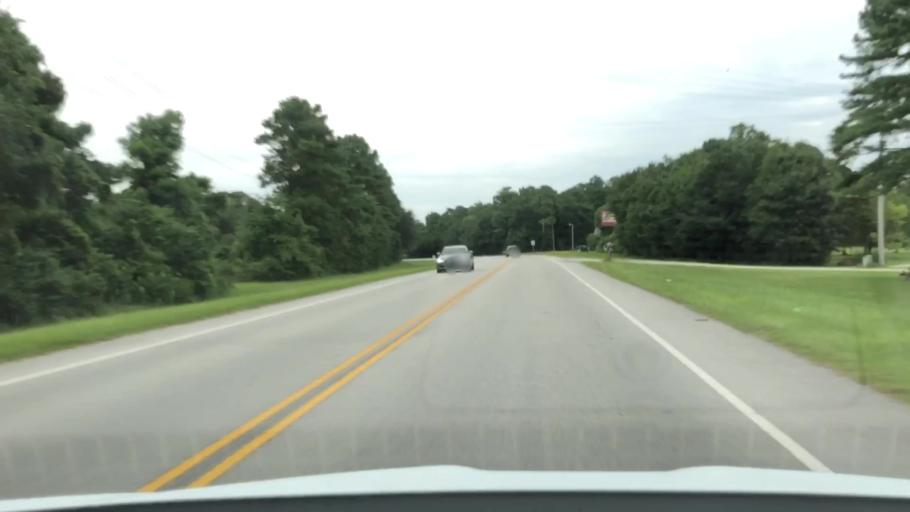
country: US
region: North Carolina
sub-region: Carteret County
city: Cape Carteret
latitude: 34.7005
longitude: -77.0681
